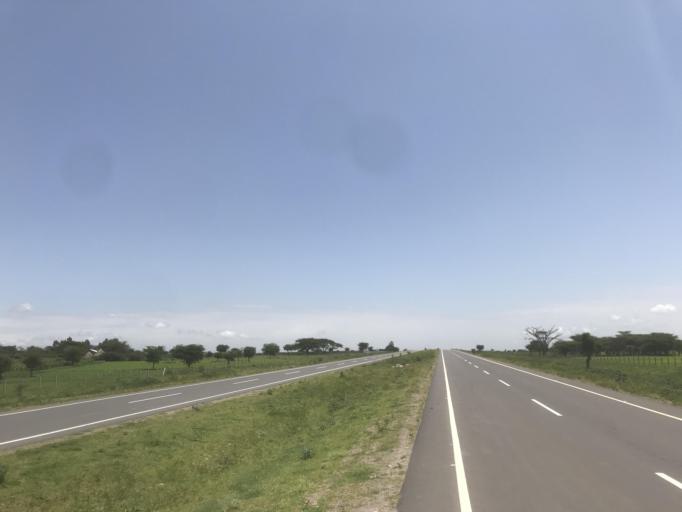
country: ET
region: Oromiya
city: Mojo
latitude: 8.3668
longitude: 38.9941
